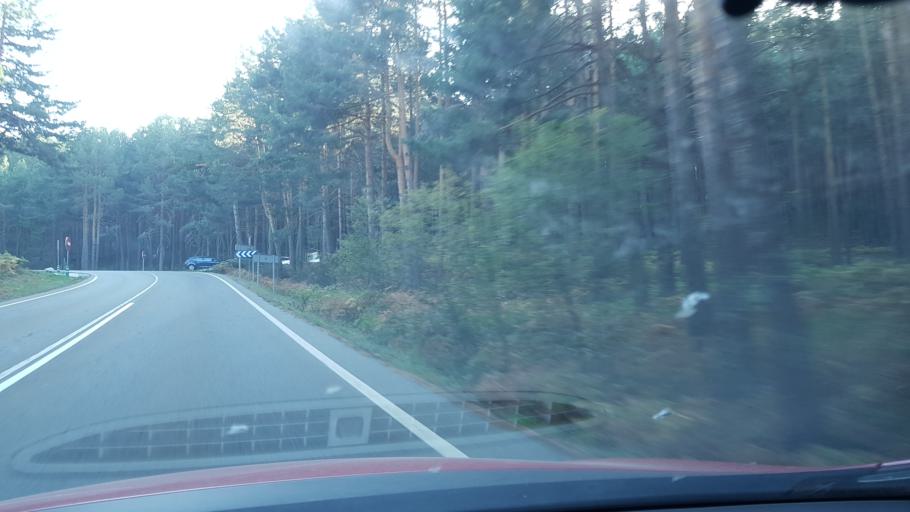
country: ES
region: Castille and Leon
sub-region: Provincia de Segovia
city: San Ildefonso
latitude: 40.8216
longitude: -4.0168
